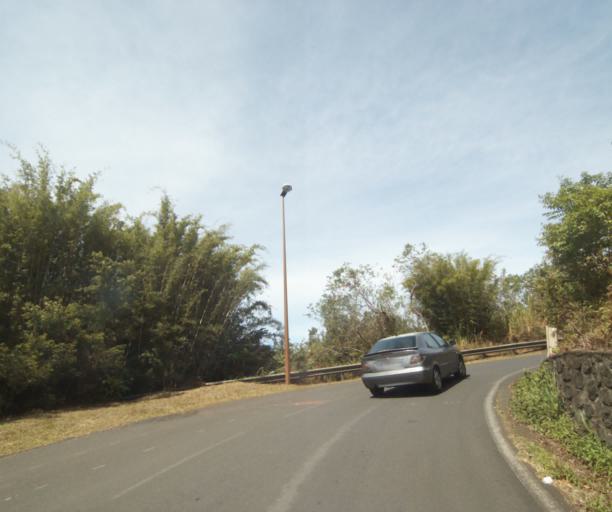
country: RE
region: Reunion
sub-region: Reunion
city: Saint-Paul
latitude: -21.0398
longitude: 55.3210
